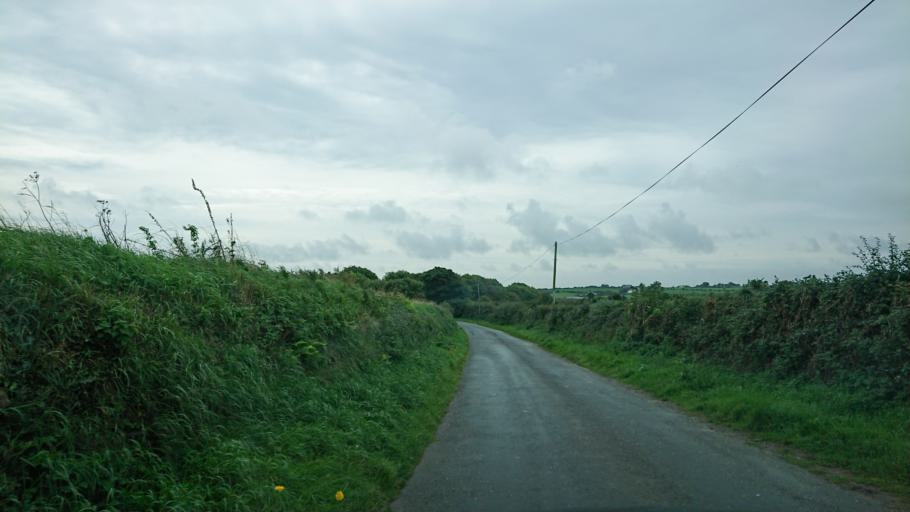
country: IE
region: Munster
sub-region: Waterford
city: Dunmore East
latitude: 52.1807
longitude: -6.9968
